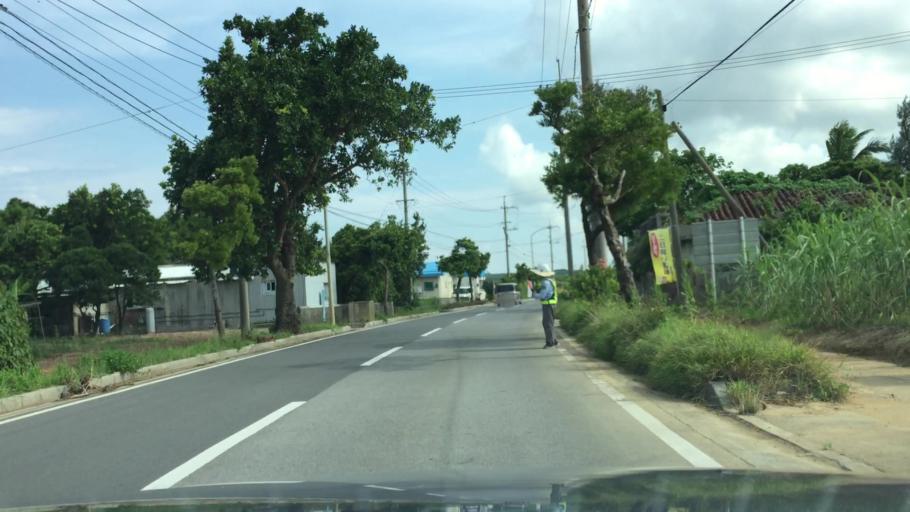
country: JP
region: Okinawa
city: Ishigaki
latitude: 24.4633
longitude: 124.2504
